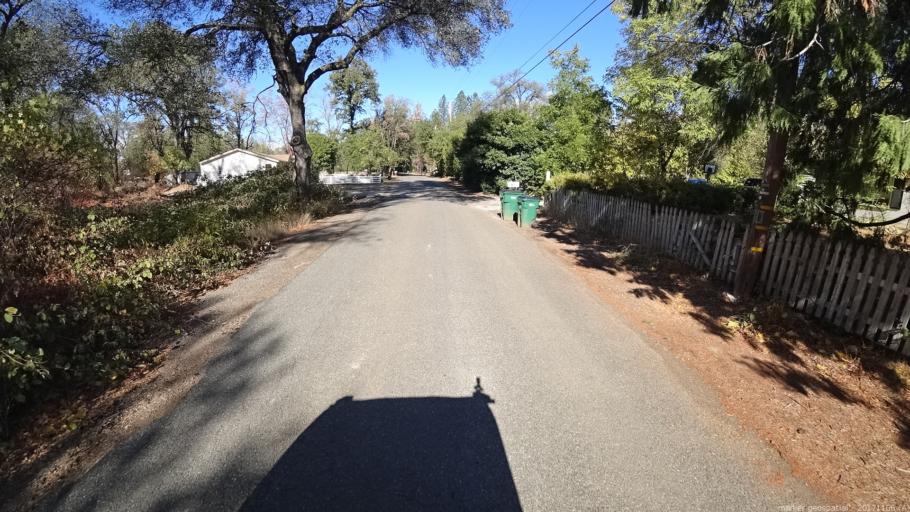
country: US
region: California
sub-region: Shasta County
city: Palo Cedro
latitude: 40.5831
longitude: -122.2959
